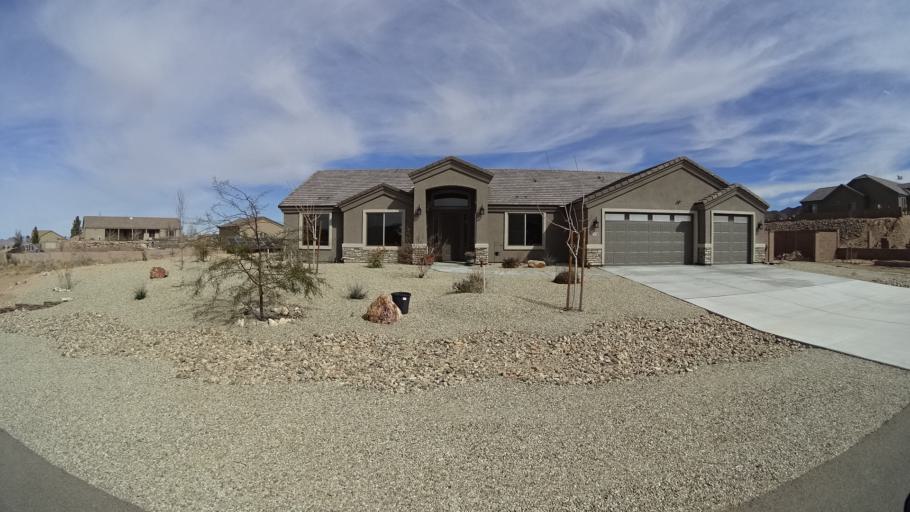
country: US
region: Arizona
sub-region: Mohave County
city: Kingman
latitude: 35.1873
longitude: -113.9779
